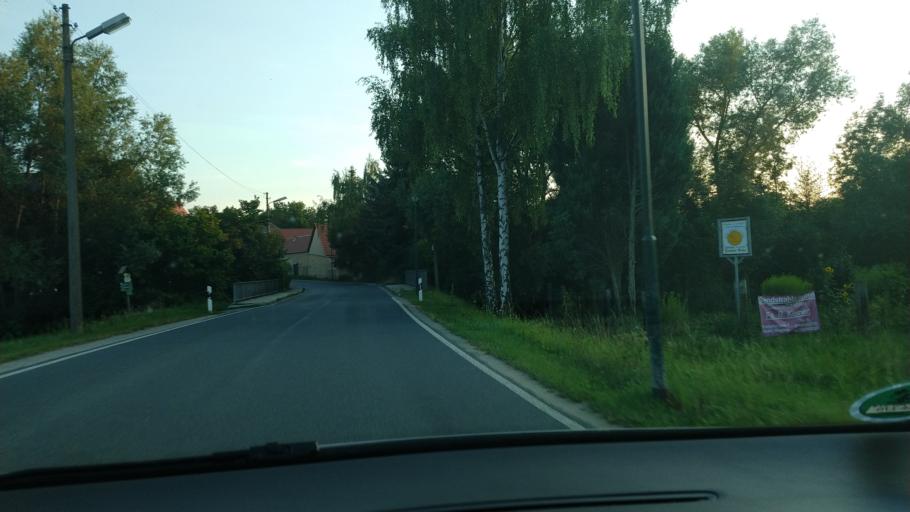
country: DE
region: Thuringia
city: Magdala
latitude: 50.9090
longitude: 11.4501
